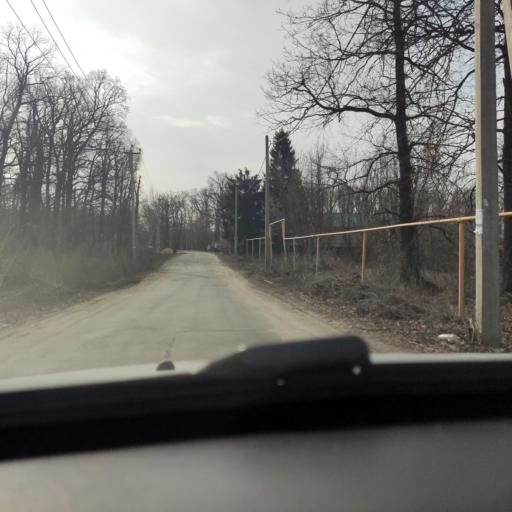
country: RU
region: Voronezj
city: Ramon'
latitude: 51.9044
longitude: 39.3641
